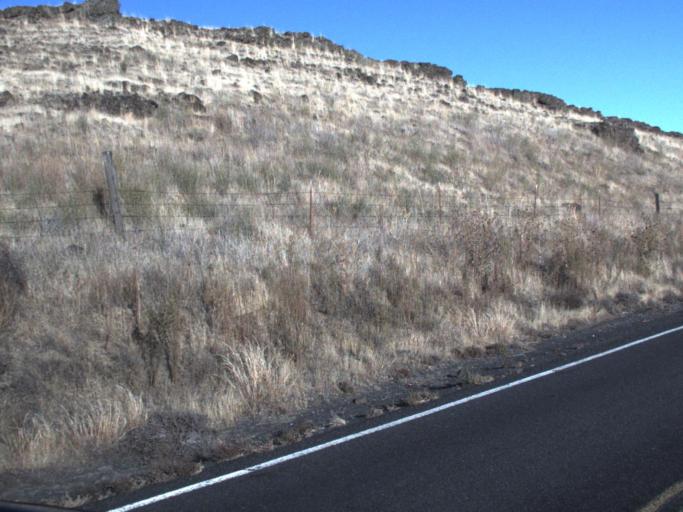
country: US
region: Washington
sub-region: Walla Walla County
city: Waitsburg
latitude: 46.6694
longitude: -118.3096
